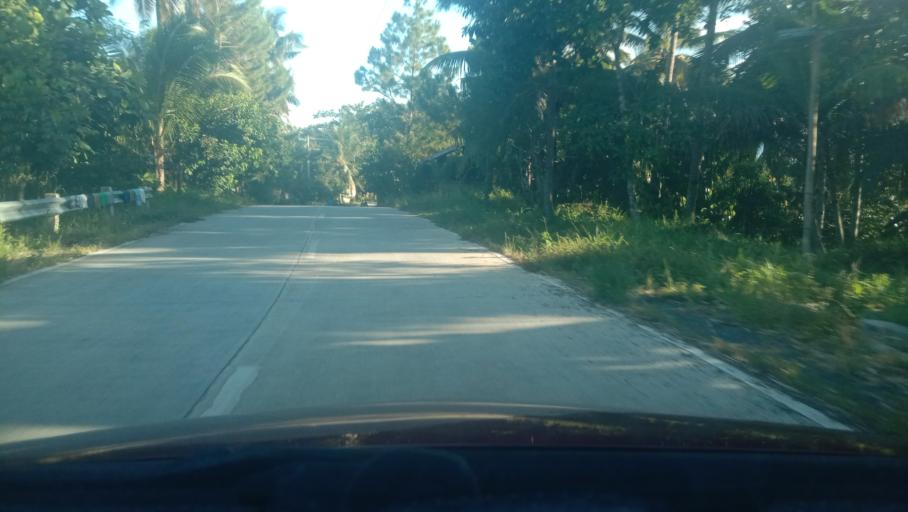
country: PH
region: Caraga
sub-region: Province of Agusan del Sur
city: San Francisco
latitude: 8.5317
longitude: 125.9620
